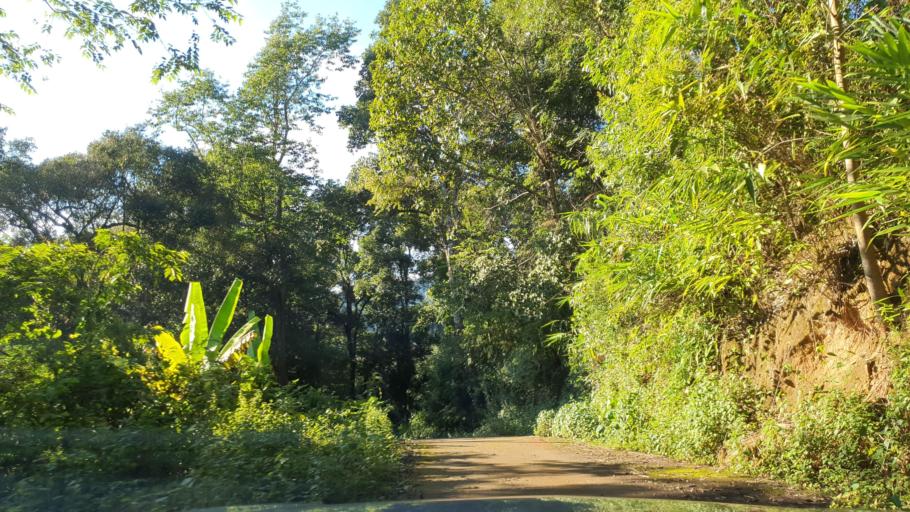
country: TH
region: Chiang Mai
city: Mae On
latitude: 18.8126
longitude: 99.3547
